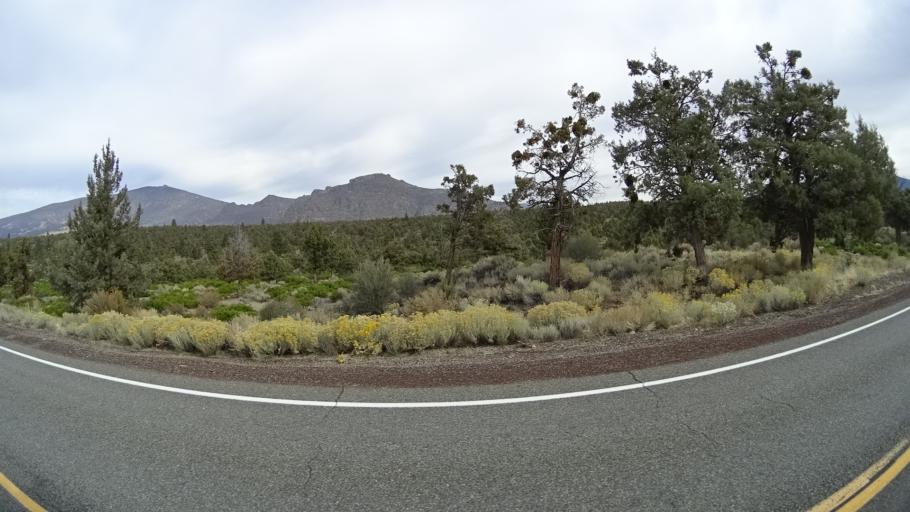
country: US
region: California
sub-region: Siskiyou County
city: Weed
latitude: 41.5550
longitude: -122.2537
